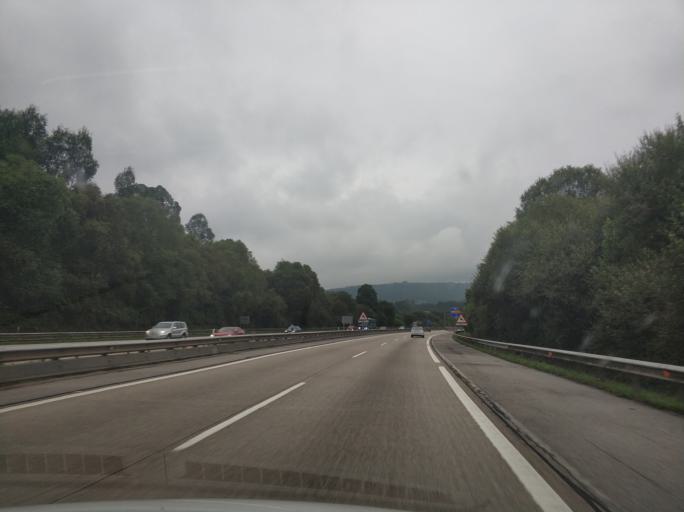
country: ES
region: Asturias
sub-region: Province of Asturias
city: Corvera de Asturias
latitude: 43.4861
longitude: -5.7897
